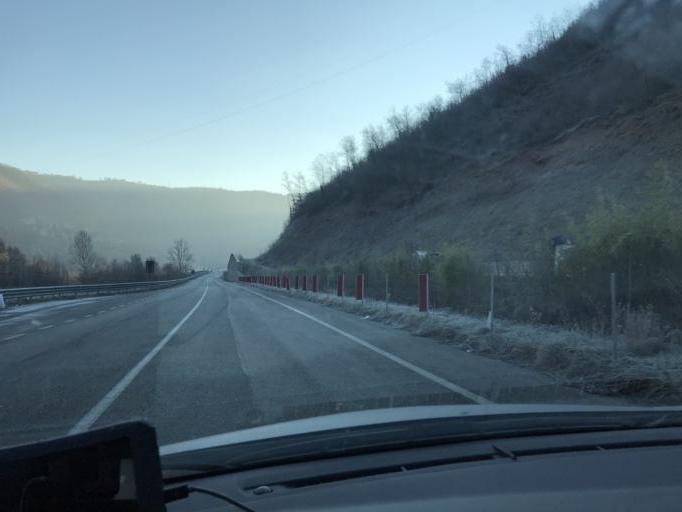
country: IT
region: Latium
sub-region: Provincia di Rieti
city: Cittaducale
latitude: 42.3528
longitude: 12.9500
